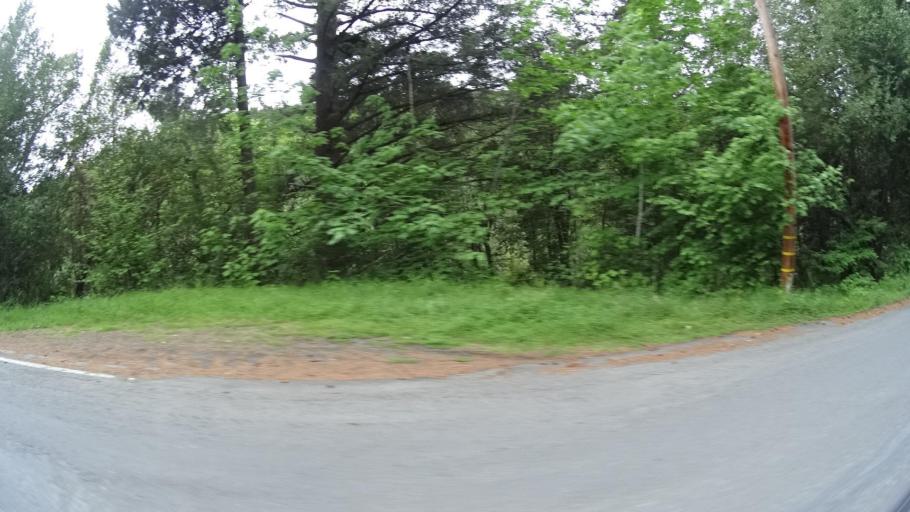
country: US
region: California
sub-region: Humboldt County
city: Willow Creek
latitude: 41.2043
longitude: -123.7525
